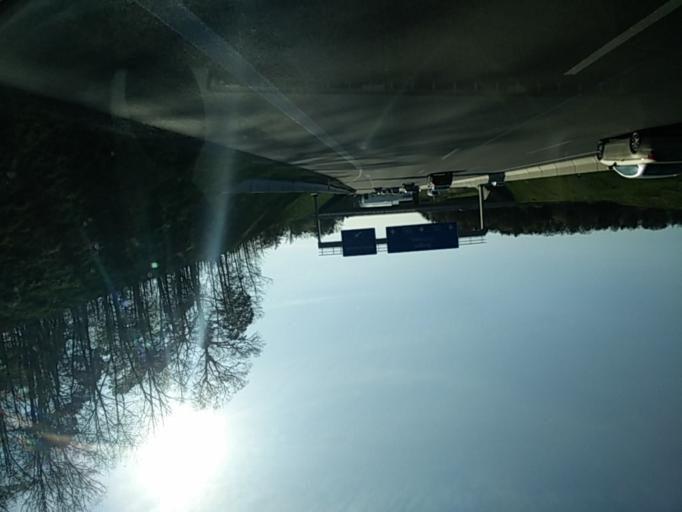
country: DE
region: Baden-Wuerttemberg
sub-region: Regierungsbezirk Stuttgart
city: Ehningen
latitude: 48.6478
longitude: 8.9443
